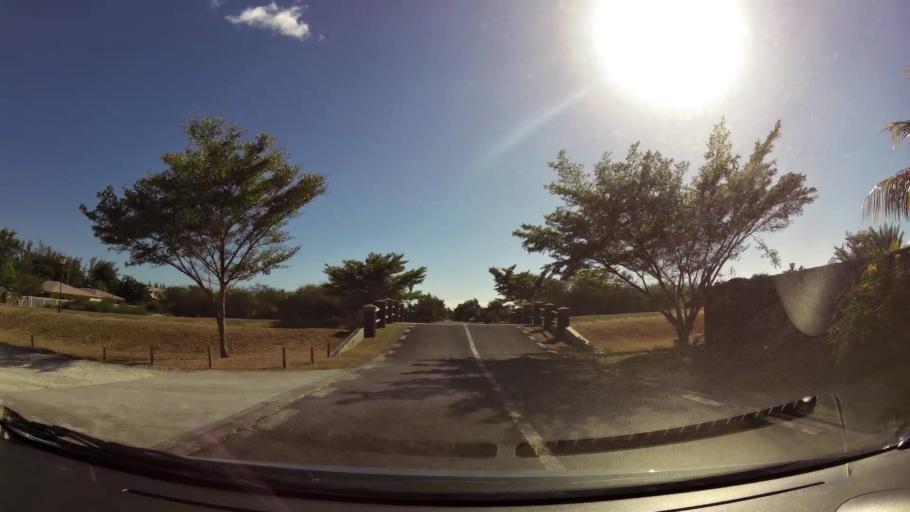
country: MU
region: Black River
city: Tamarin
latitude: -20.3419
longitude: 57.3652
